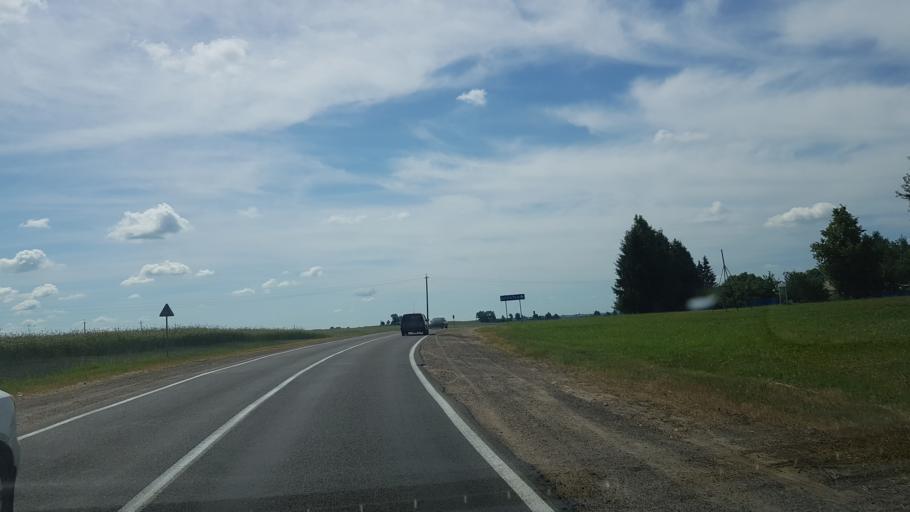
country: BY
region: Vitebsk
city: Dubrowna
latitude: 54.6515
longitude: 30.6660
